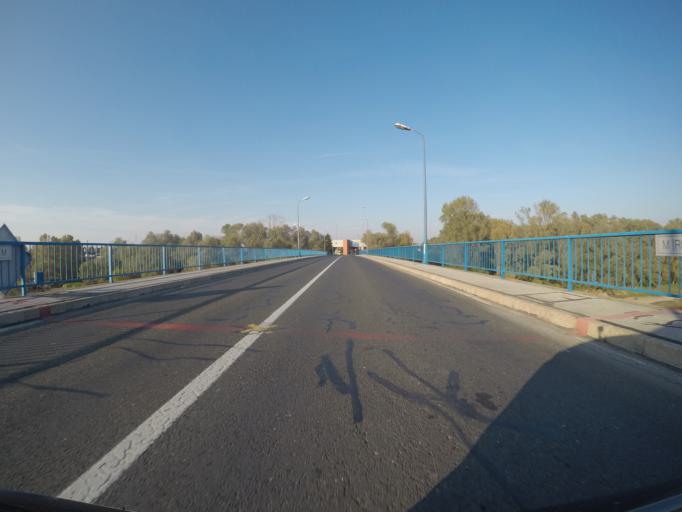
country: HU
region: Somogy
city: Barcs
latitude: 45.9457
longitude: 17.4618
